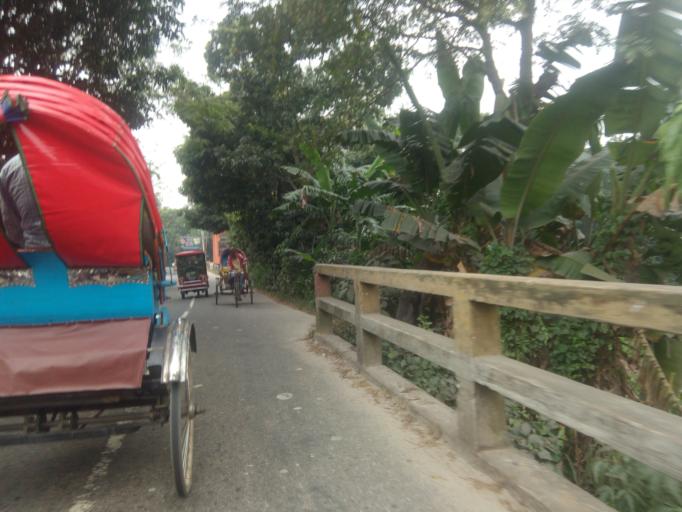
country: BD
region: Dhaka
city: Narayanganj
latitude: 23.5292
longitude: 90.4788
